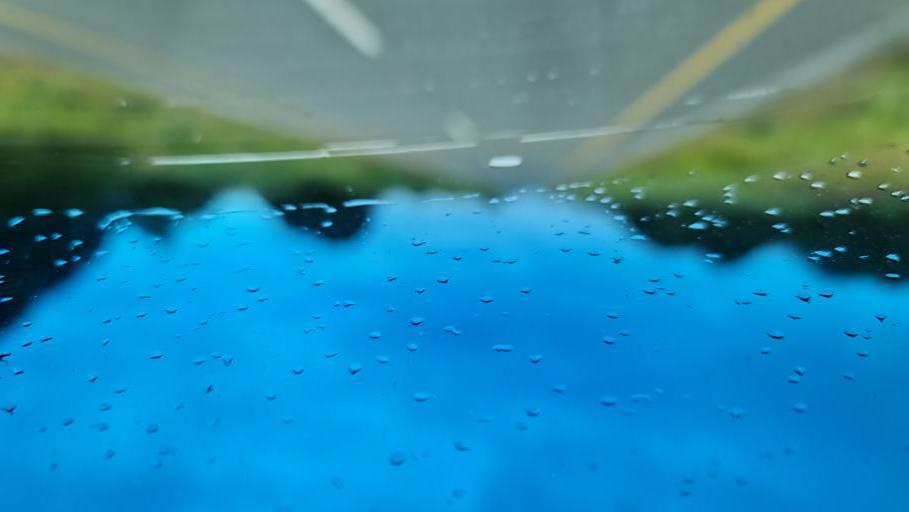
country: MZ
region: Nampula
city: Nampula
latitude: -15.5244
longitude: 39.3327
